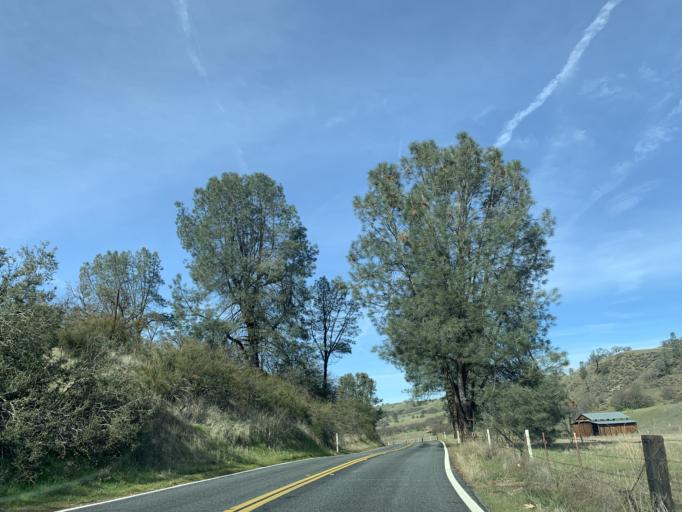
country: US
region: California
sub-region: Monterey County
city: Greenfield
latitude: 36.5065
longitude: -121.1097
